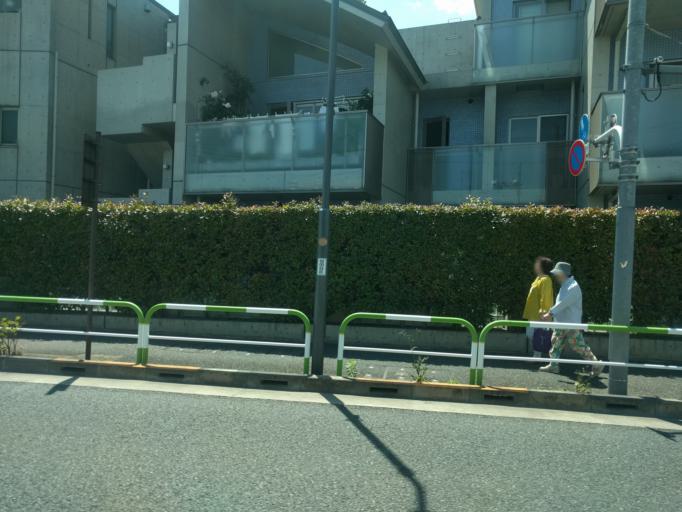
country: JP
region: Tokyo
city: Mitaka-shi
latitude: 35.6623
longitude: 139.6240
